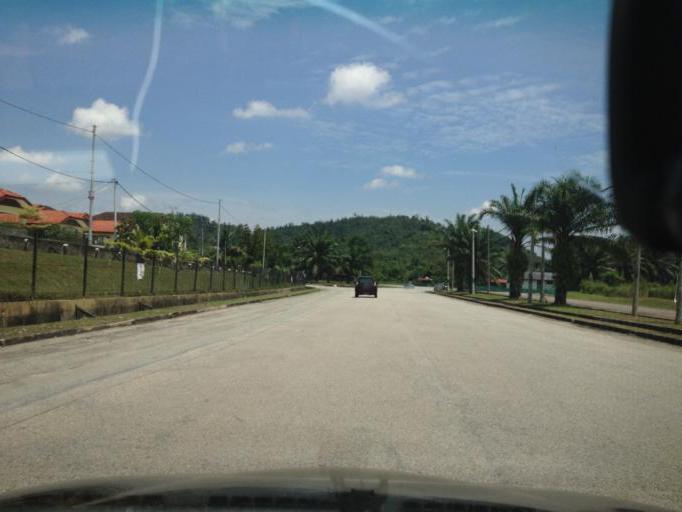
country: MY
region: Kedah
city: Sungai Petani
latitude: 5.6355
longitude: 100.5557
